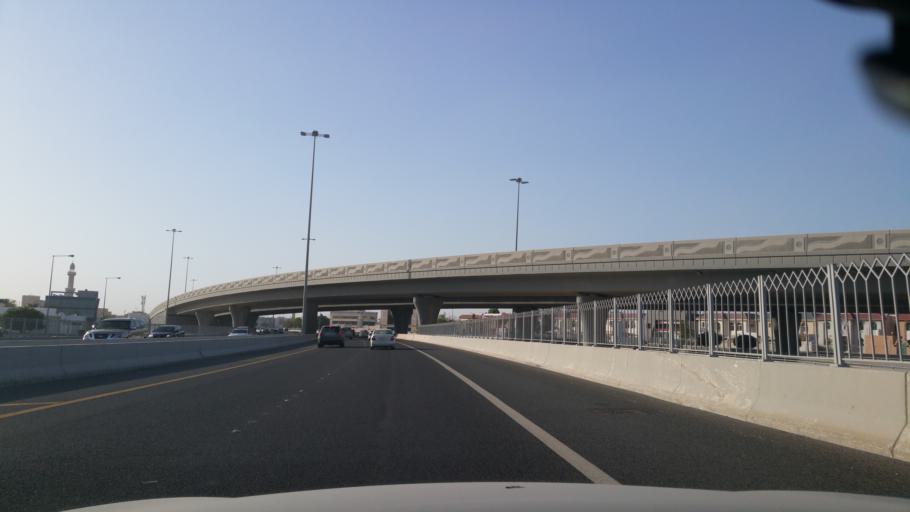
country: QA
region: Baladiyat ad Dawhah
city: Doha
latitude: 25.2535
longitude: 51.5077
